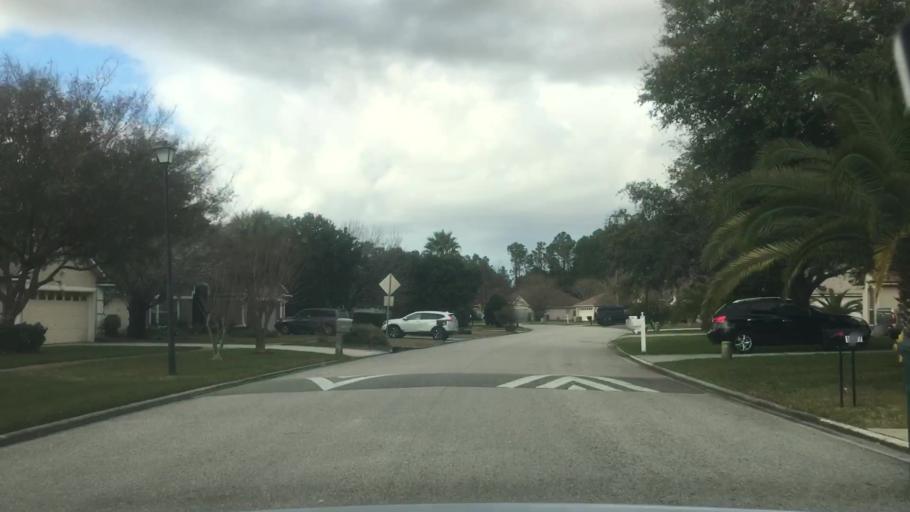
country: US
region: Florida
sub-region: Duval County
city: Atlantic Beach
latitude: 30.3177
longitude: -81.5065
